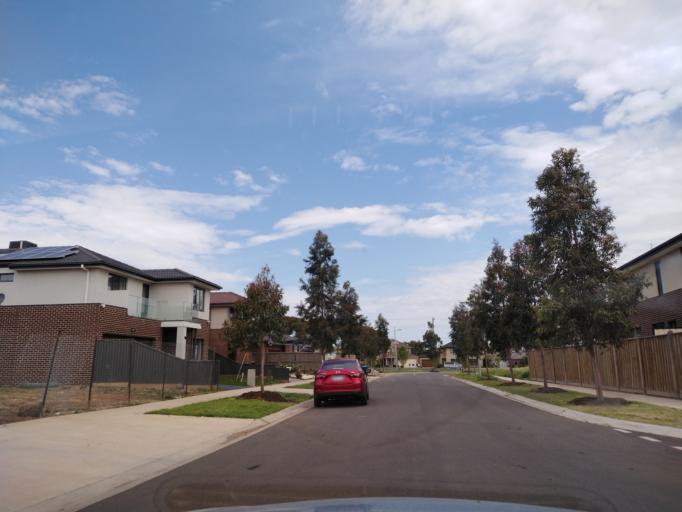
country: AU
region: Victoria
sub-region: Wyndham
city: Williams Landing
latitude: -37.8504
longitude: 144.7150
